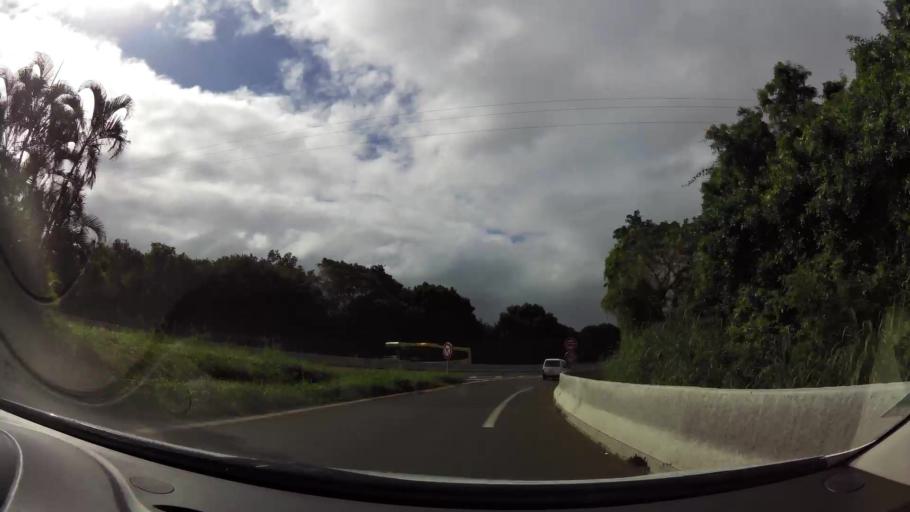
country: RE
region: Reunion
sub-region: Reunion
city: Sainte-Marie
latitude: -20.8981
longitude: 55.5741
